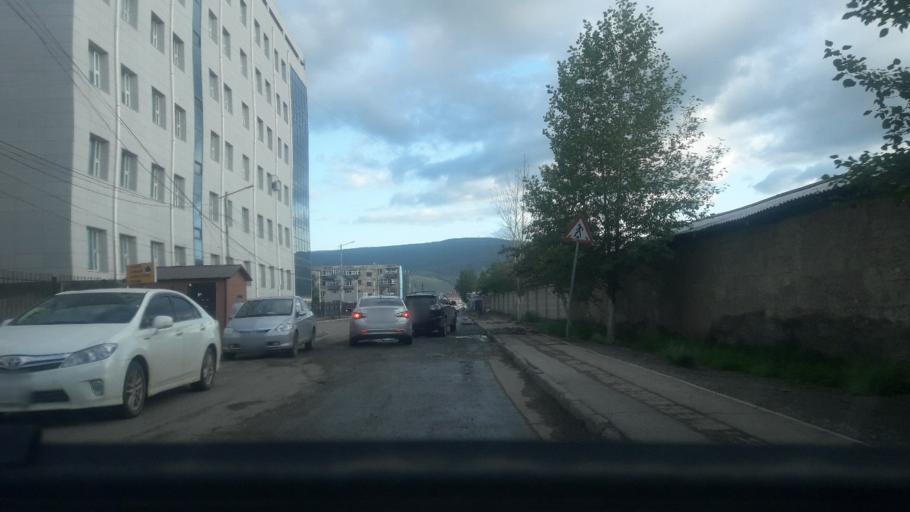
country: MN
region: Ulaanbaatar
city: Ulaanbaatar
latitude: 47.9155
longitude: 106.9945
